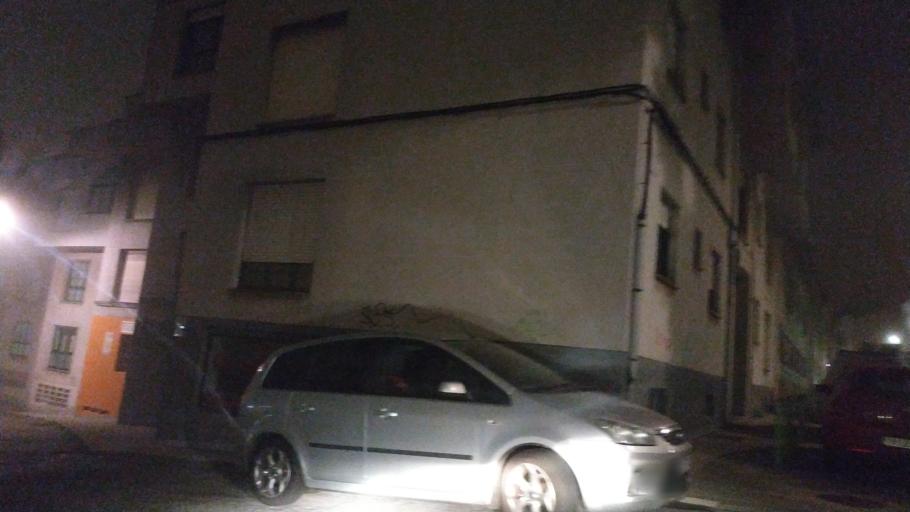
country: ES
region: Galicia
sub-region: Provincia da Coruna
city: Culleredo
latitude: 43.3289
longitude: -8.3941
